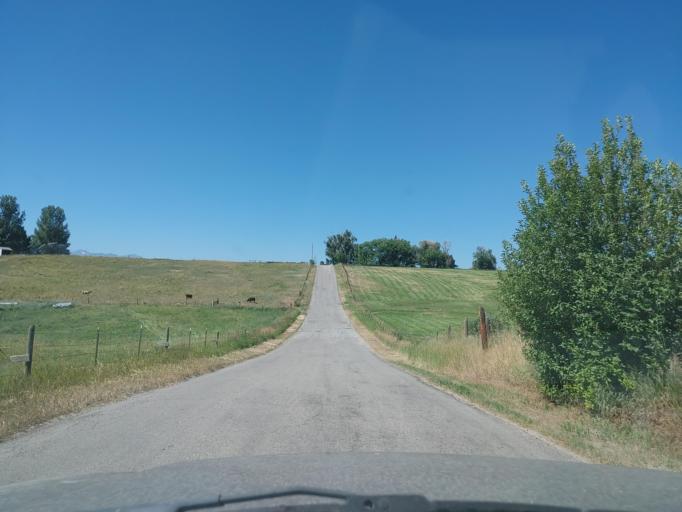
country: US
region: Montana
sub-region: Ravalli County
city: Hamilton
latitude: 46.3135
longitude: -114.0613
